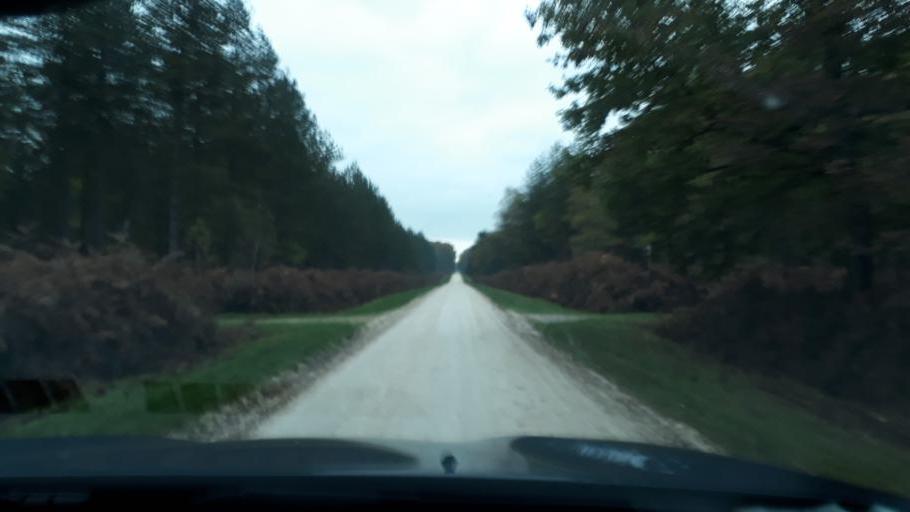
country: FR
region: Centre
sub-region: Departement du Loiret
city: Ouzouer-sur-Loire
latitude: 47.8353
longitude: 2.4618
